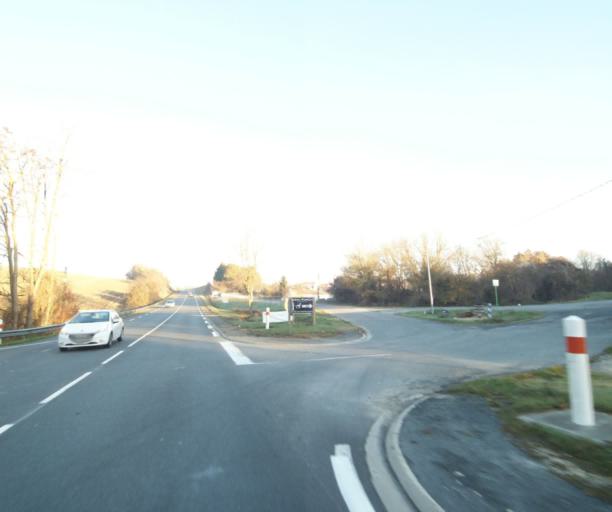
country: FR
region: Poitou-Charentes
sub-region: Departement de la Charente-Maritime
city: Cherac
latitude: 45.7185
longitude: -0.4948
